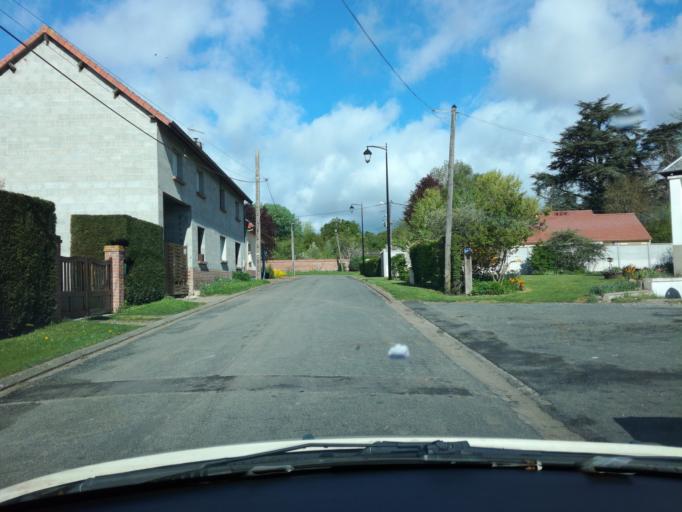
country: FR
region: Picardie
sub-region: Departement de la Somme
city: Poix-de-Picardie
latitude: 49.8202
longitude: 2.0164
